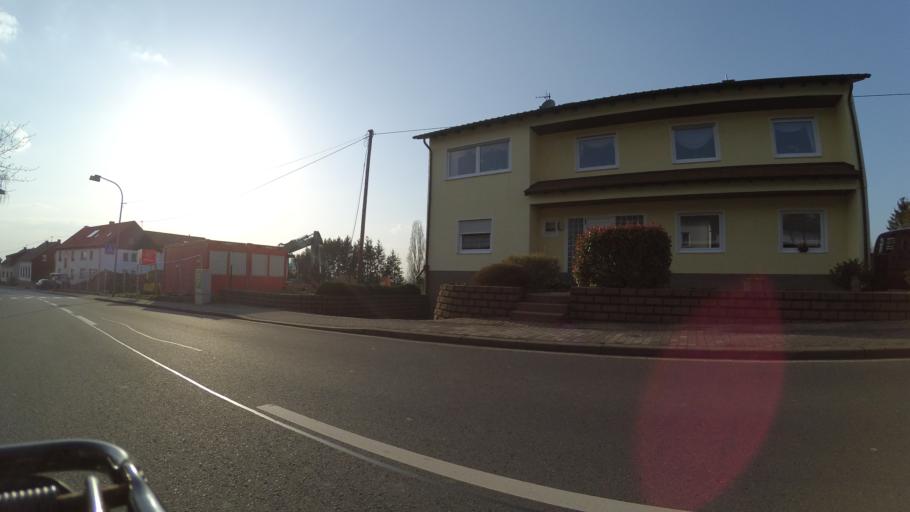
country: DE
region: Saarland
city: Merchweiler
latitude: 49.3461
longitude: 7.0021
